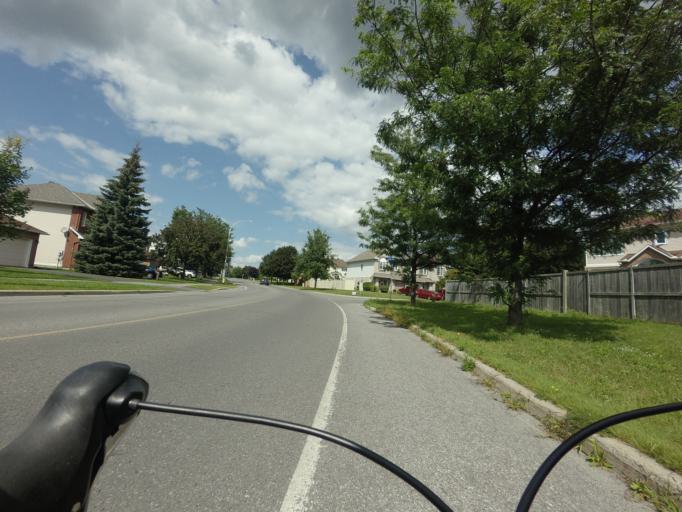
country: CA
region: Ontario
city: Bells Corners
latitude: 45.2788
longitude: -75.8465
